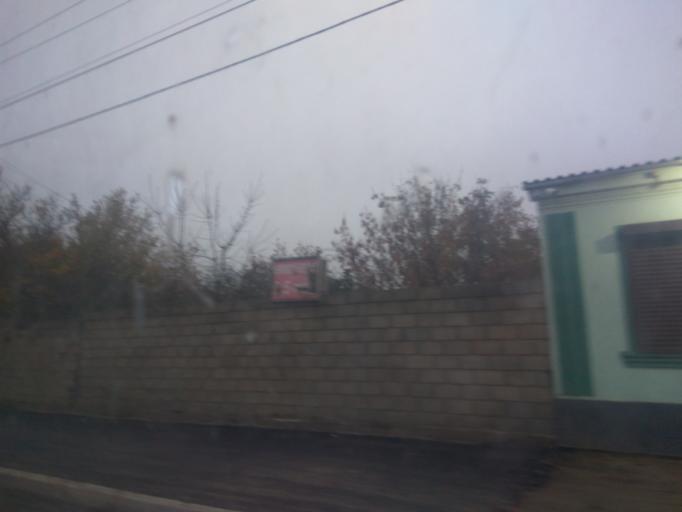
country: RU
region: Dagestan
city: Kyakhulay
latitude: 42.9749
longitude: 47.4760
